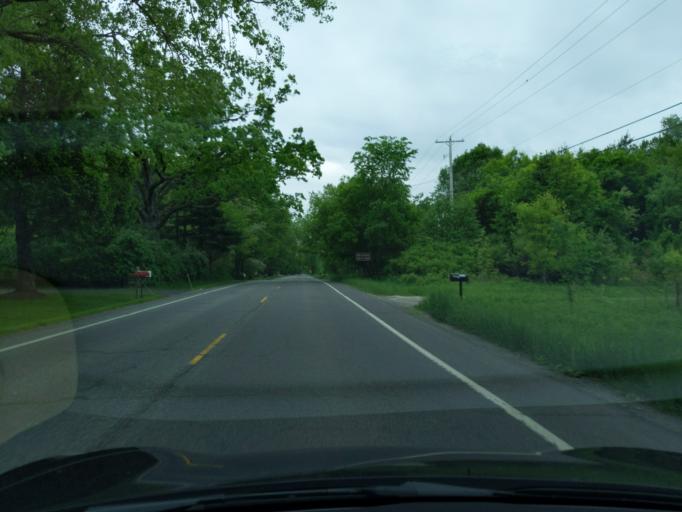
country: US
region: Michigan
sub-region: Ingham County
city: Haslett
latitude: 42.7342
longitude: -84.3635
